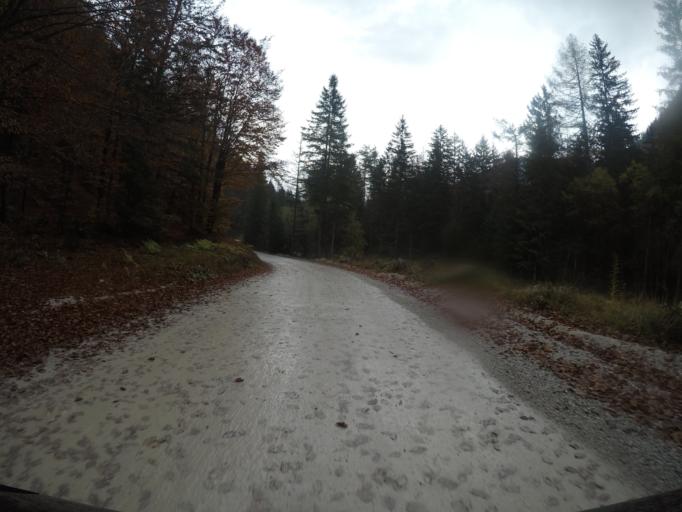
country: SI
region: Kranjska Gora
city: Mojstrana
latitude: 46.4448
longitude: 13.9123
